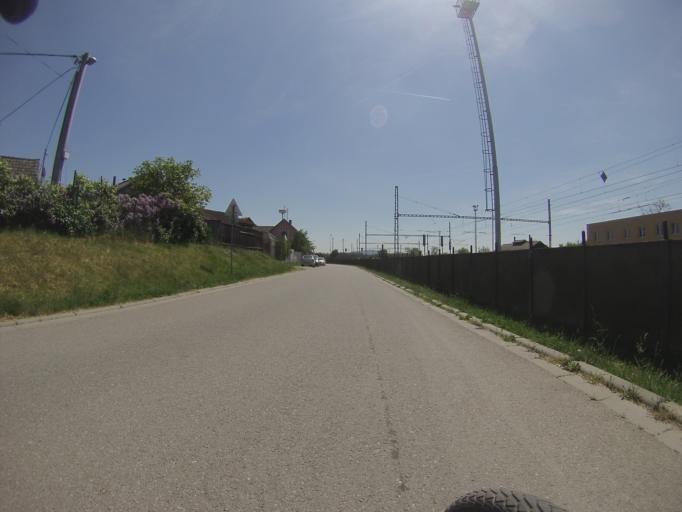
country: CZ
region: South Moravian
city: Vranovice
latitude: 48.9668
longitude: 16.6032
